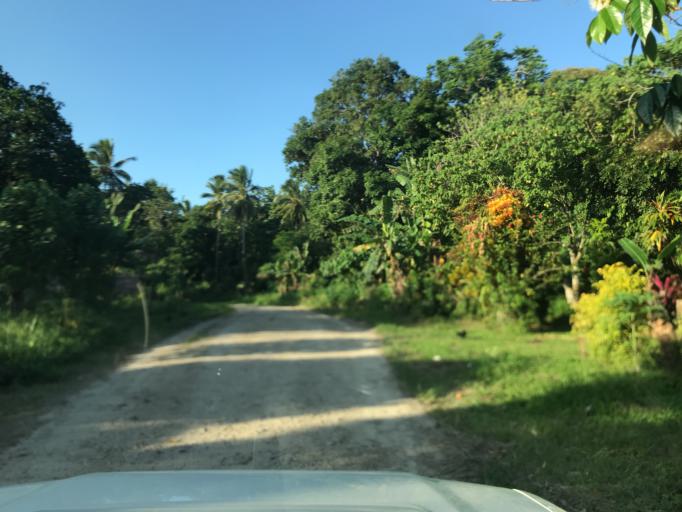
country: VU
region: Sanma
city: Luganville
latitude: -15.5906
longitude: 166.8991
